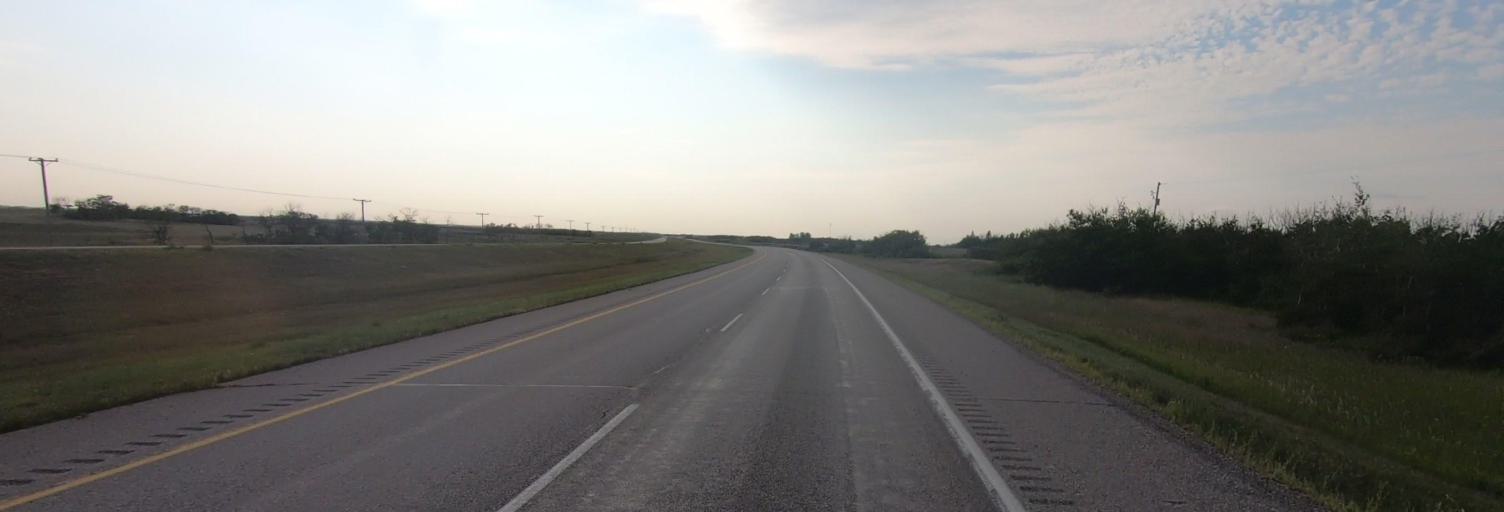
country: CA
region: Saskatchewan
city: Melville
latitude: 50.3802
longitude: -102.6309
